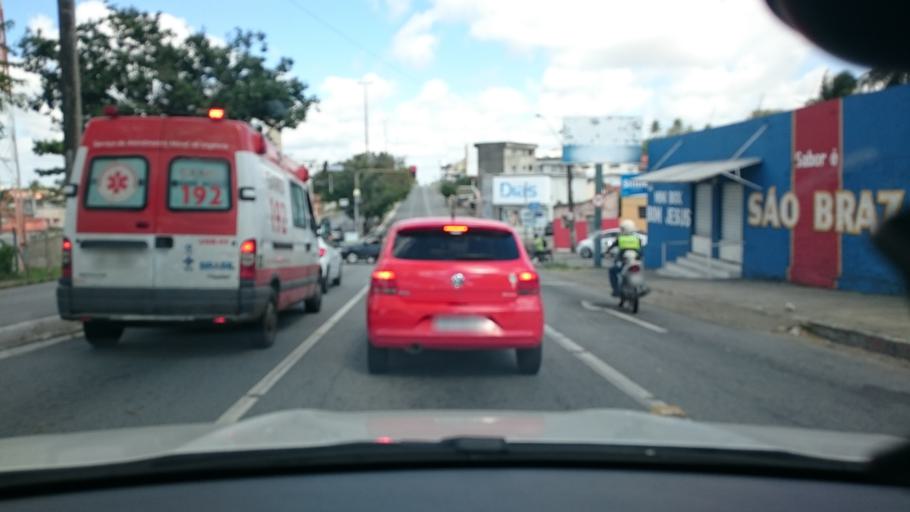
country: BR
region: Paraiba
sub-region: Campina Grande
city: Campina Grande
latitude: -7.2253
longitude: -35.8966
